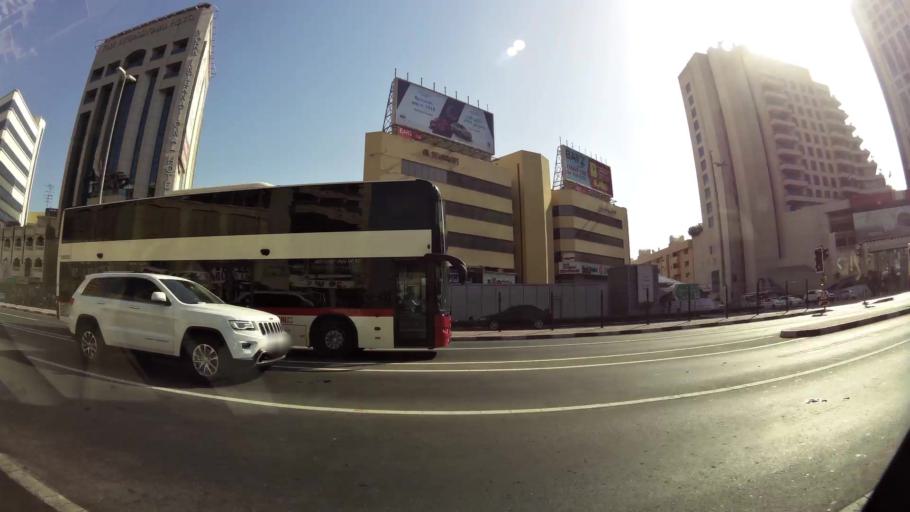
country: AE
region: Ash Shariqah
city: Sharjah
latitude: 25.2583
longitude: 55.2972
